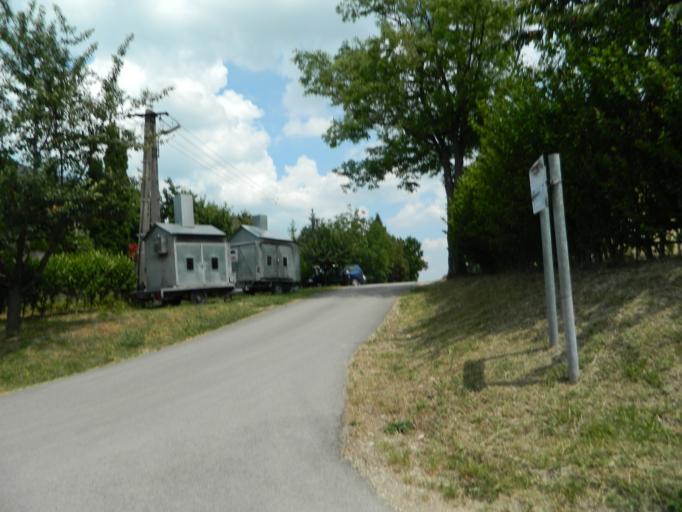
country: HU
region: Somogy
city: Balatonfoldvar
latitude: 46.8417
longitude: 17.8677
